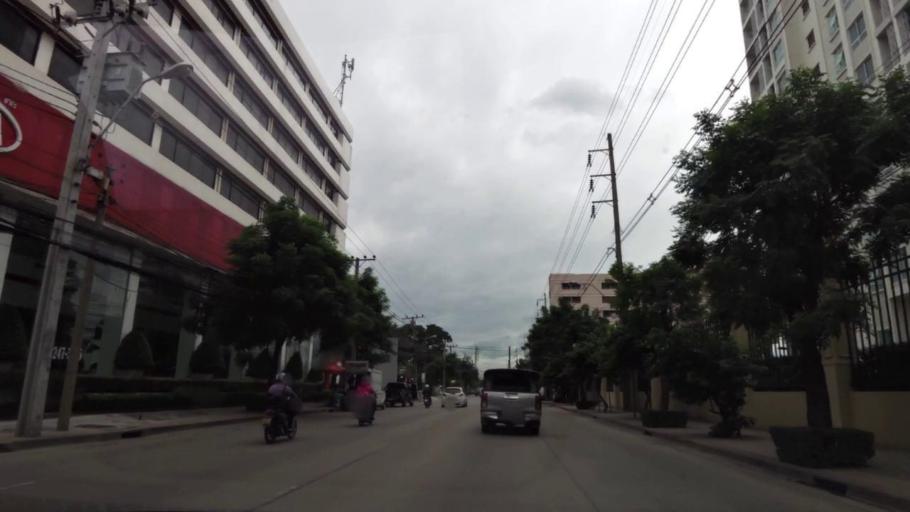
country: TH
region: Bangkok
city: Huai Khwang
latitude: 13.7666
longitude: 100.5821
